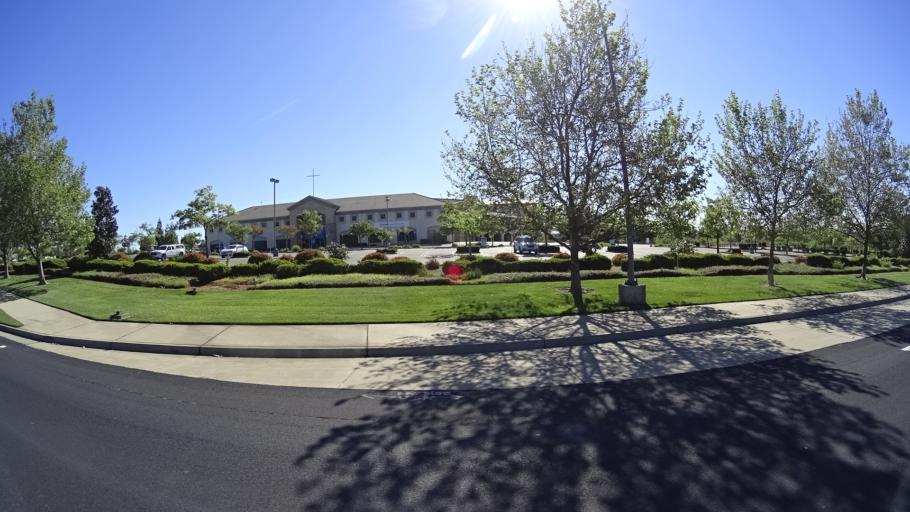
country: US
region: California
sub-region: Placer County
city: Rocklin
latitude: 38.7905
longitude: -121.2692
